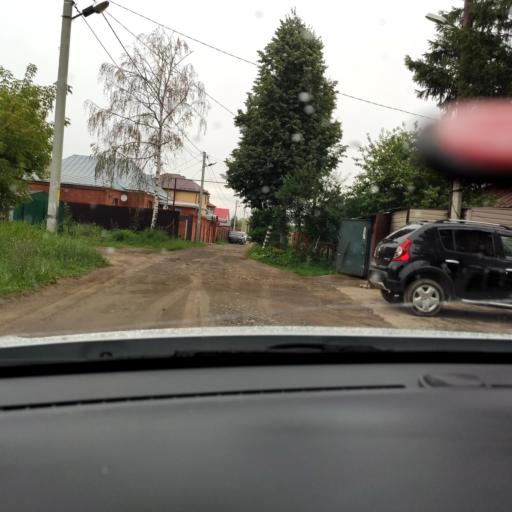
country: RU
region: Tatarstan
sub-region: Gorod Kazan'
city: Kazan
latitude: 55.8430
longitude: 49.1962
